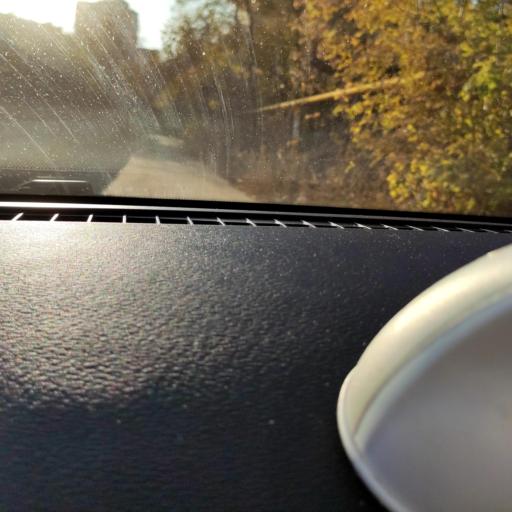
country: RU
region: Samara
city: Samara
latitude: 53.2158
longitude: 50.2147
